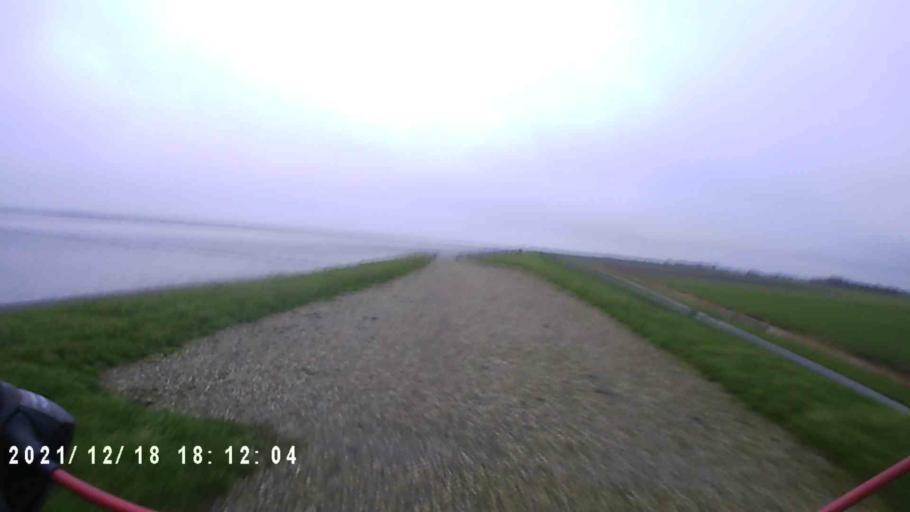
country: NL
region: Friesland
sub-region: Gemeente Dongeradeel
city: Ternaard
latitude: 53.3905
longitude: 5.9476
